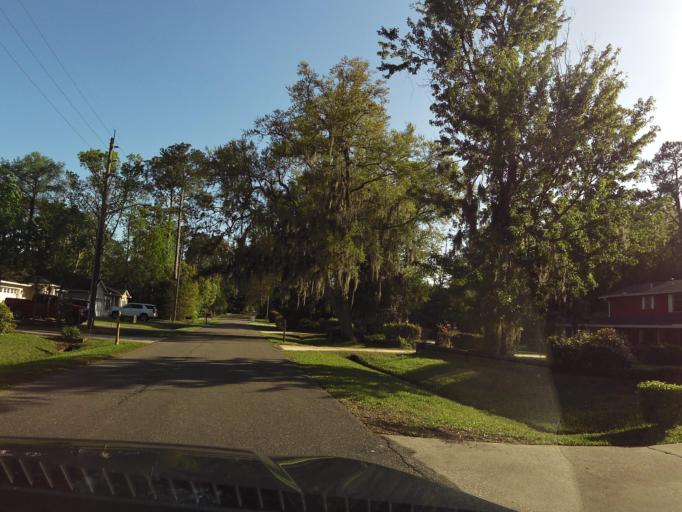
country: US
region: Florida
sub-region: Duval County
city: Jacksonville
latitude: 30.2729
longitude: -81.5816
